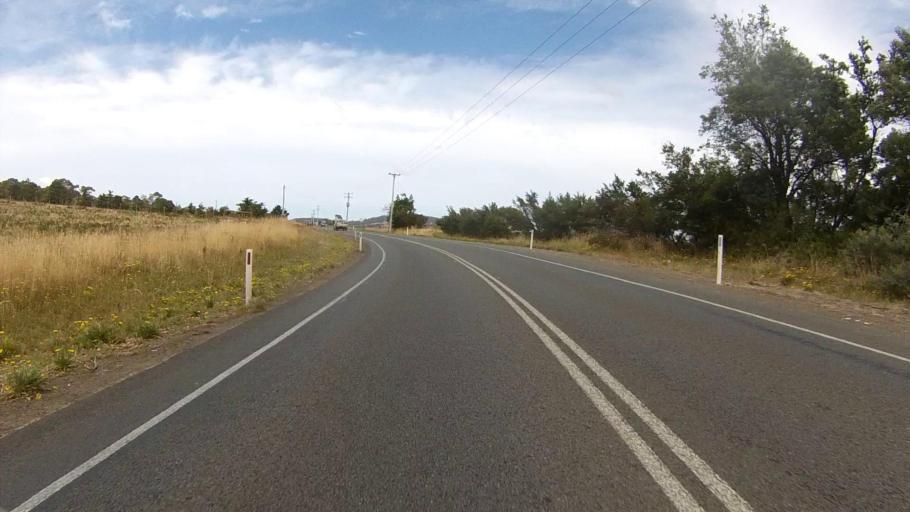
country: AU
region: Tasmania
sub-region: Clarence
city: Sandford
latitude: -42.9301
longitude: 147.4910
